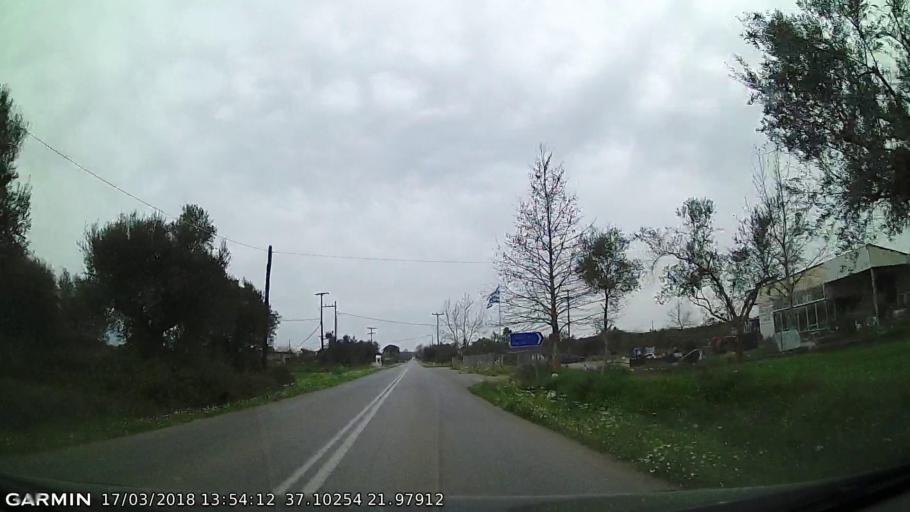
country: GR
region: Peloponnese
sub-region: Nomos Messinias
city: Aris
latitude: 37.1026
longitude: 21.9791
